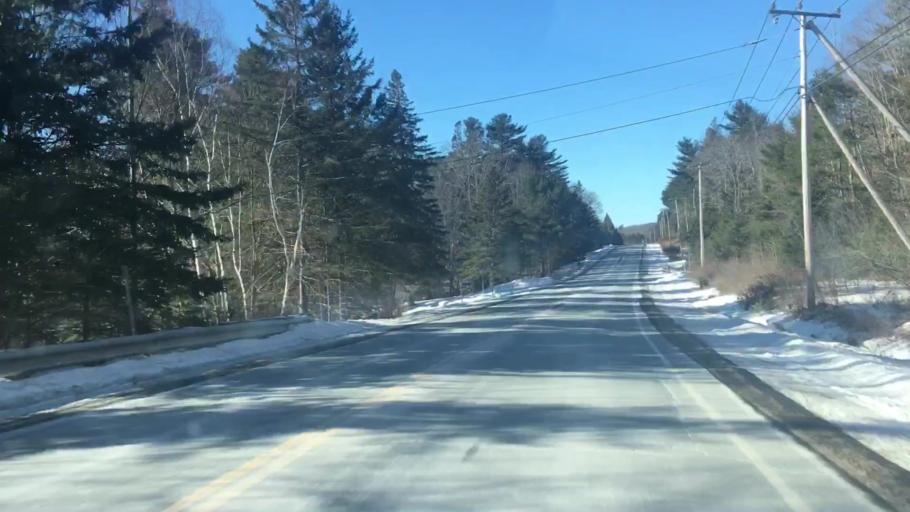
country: US
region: Maine
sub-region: Hancock County
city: Surry
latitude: 44.4949
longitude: -68.4791
